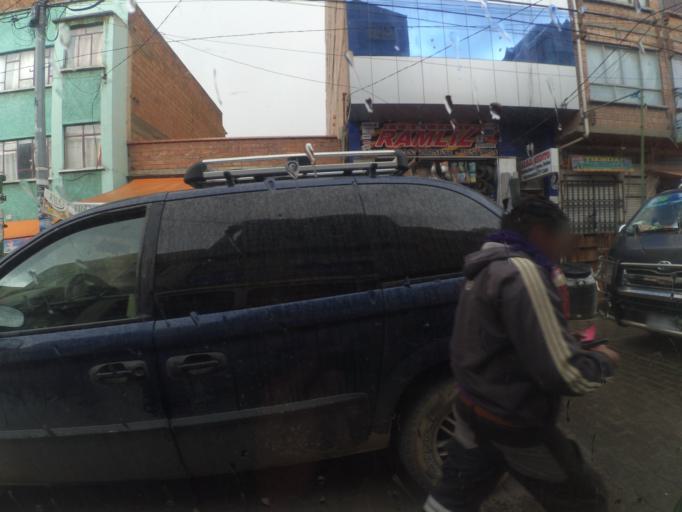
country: BO
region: La Paz
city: La Paz
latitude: -16.5103
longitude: -68.1634
